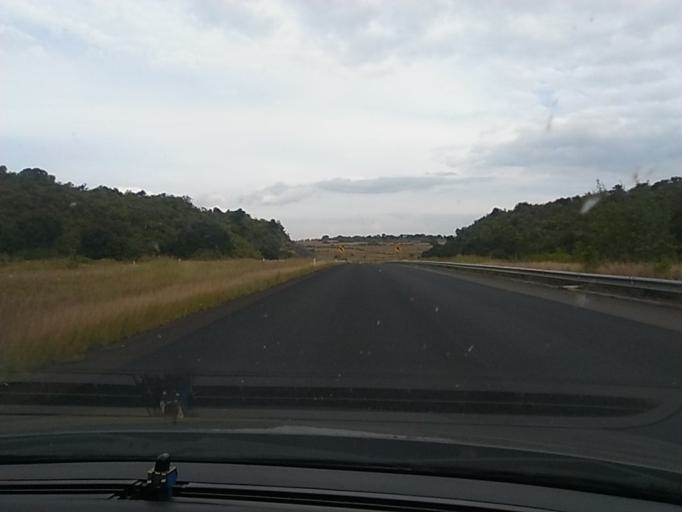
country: MX
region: Mexico
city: Huaniqueo de Morales
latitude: 19.8843
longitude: -101.4484
